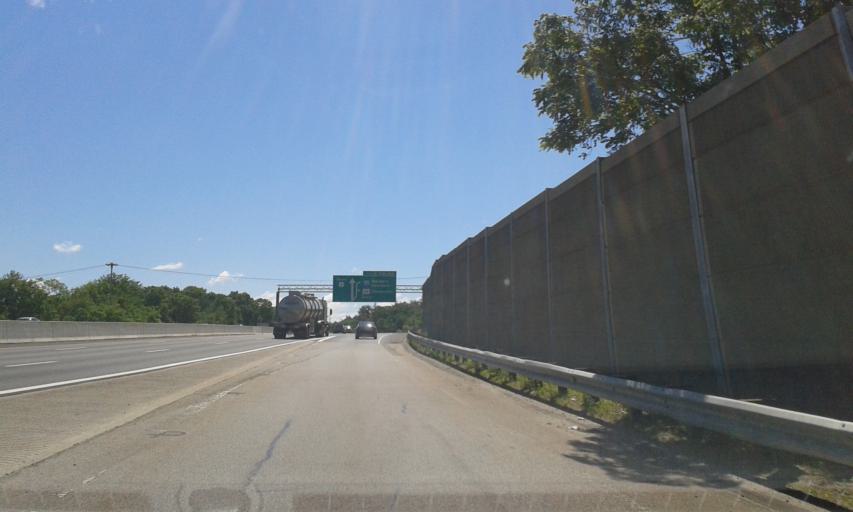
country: US
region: Massachusetts
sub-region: Middlesex County
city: Chelmsford
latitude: 42.6213
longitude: -71.3618
